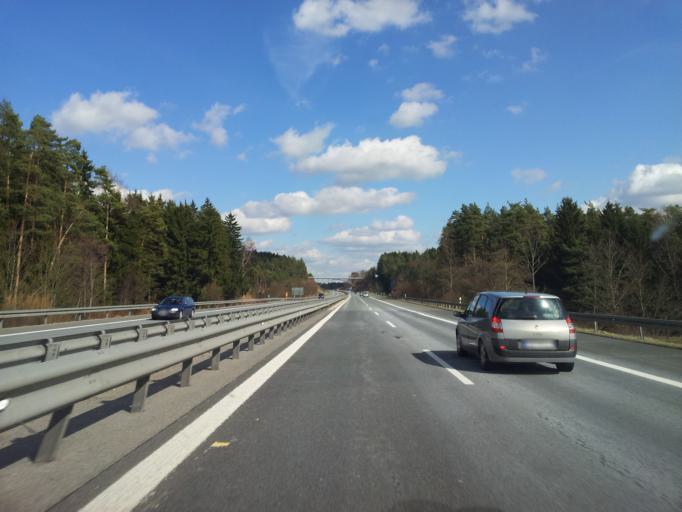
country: DE
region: Bavaria
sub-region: Upper Franconia
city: Wattendorf
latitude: 49.9909
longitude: 11.1371
